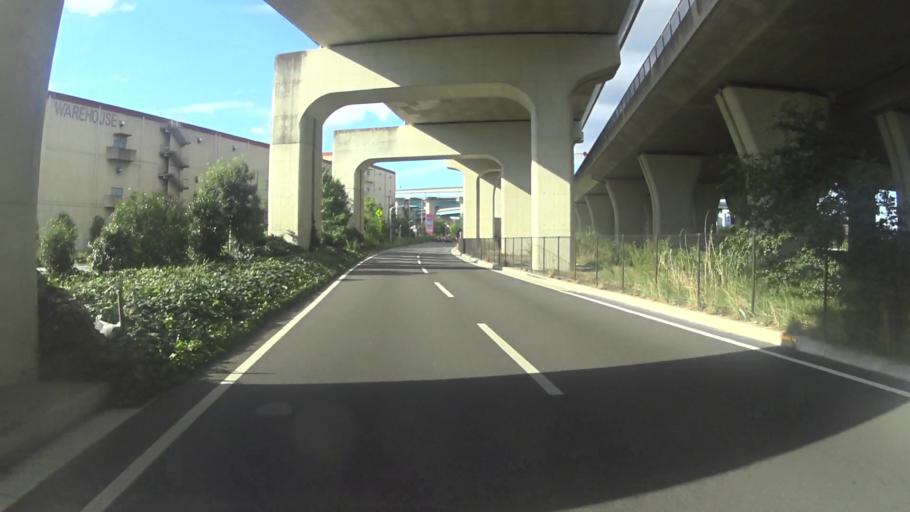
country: JP
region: Kyoto
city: Yawata
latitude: 34.8920
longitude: 135.7493
